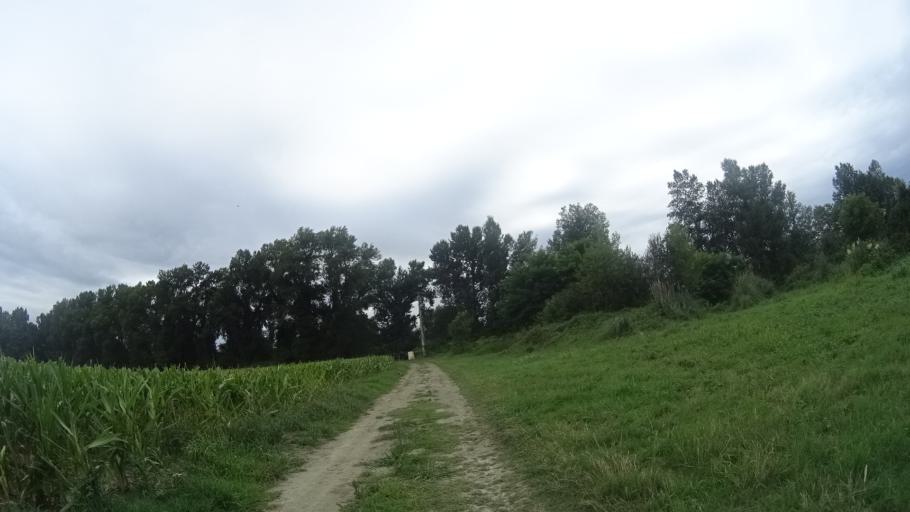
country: FR
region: Aquitaine
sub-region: Departement des Pyrenees-Atlantiques
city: Orthez
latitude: 43.4642
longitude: -0.7222
